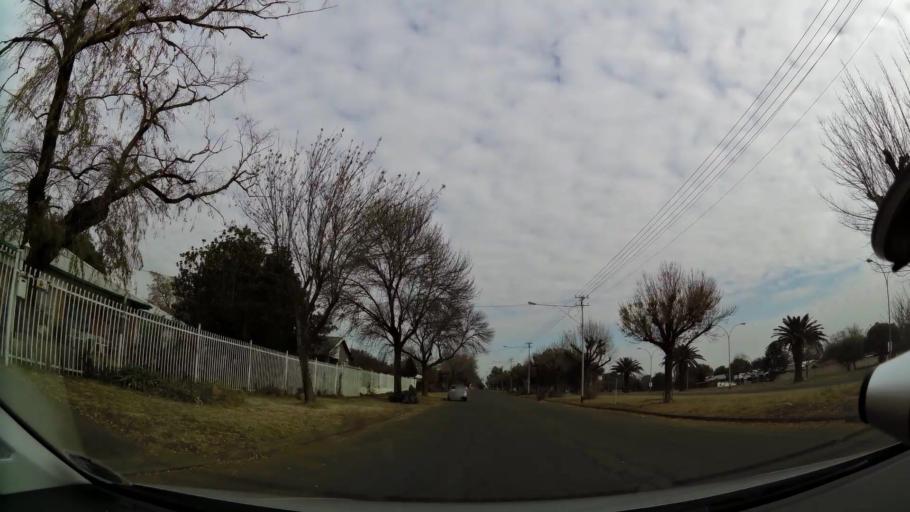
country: ZA
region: Orange Free State
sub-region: Mangaung Metropolitan Municipality
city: Bloemfontein
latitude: -29.1269
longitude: 26.1719
